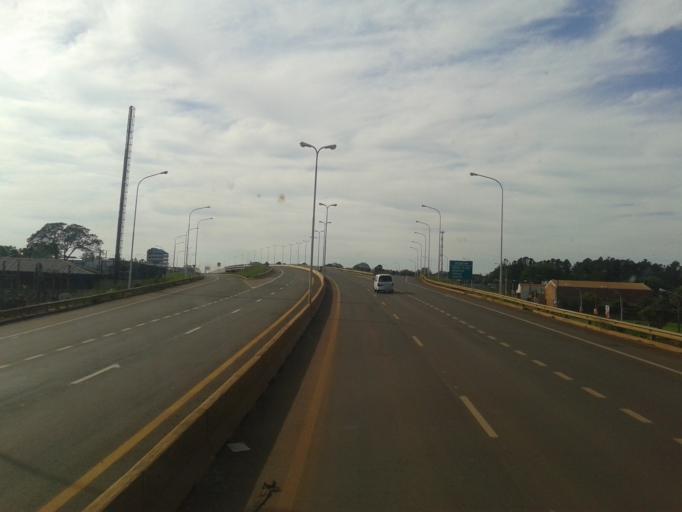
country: AR
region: Misiones
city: Garupa
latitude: -27.4519
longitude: -55.8659
